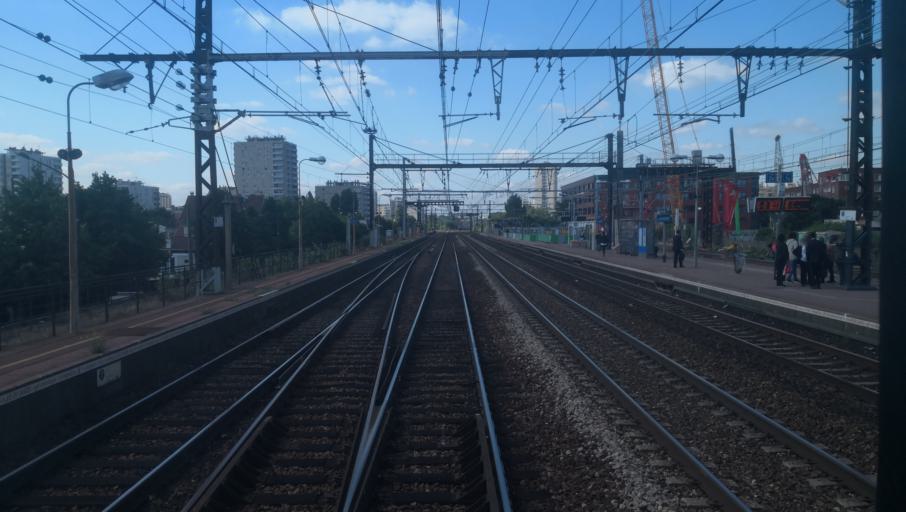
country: FR
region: Ile-de-France
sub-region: Departement du Val-de-Marne
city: Alfortville
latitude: 48.7882
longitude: 2.4322
